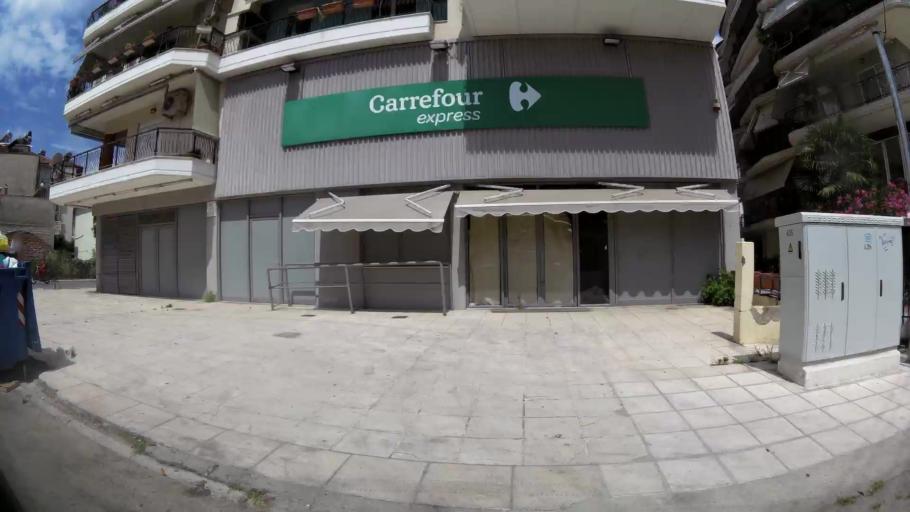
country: GR
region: Central Macedonia
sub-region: Nomos Pierias
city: Katerini
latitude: 40.2739
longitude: 22.4987
